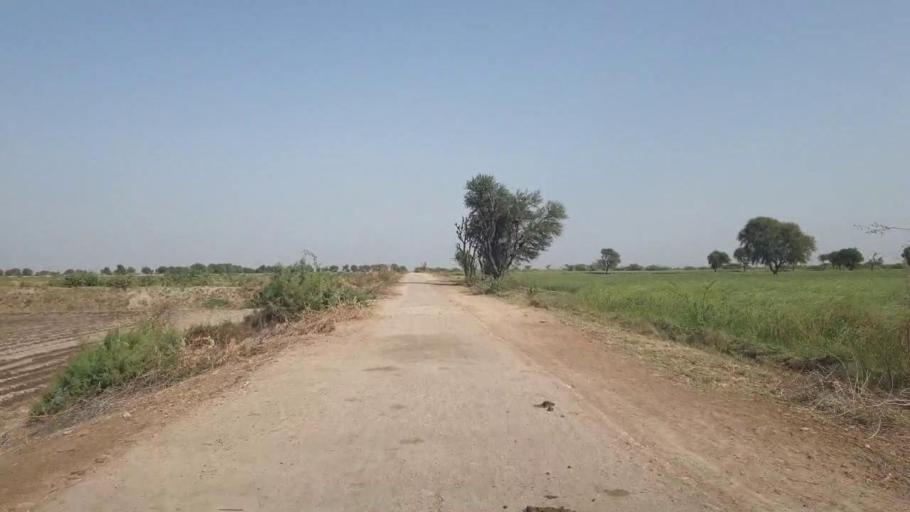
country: PK
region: Sindh
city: Dhoro Naro
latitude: 25.4419
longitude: 69.5434
